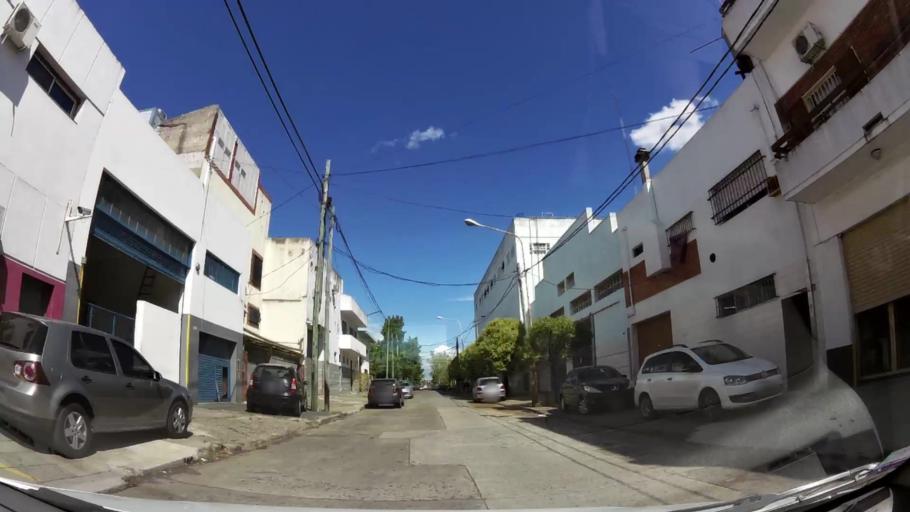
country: AR
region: Buenos Aires
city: San Justo
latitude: -34.6571
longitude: -58.5322
